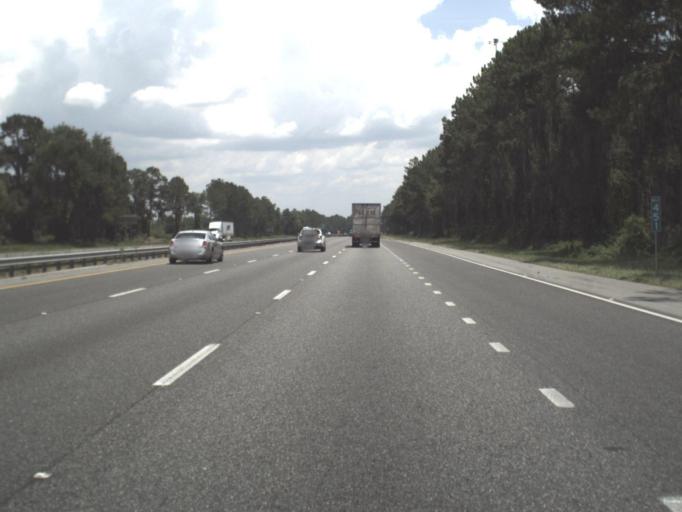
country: US
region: Florida
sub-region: Hamilton County
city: Jasper
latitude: 30.4457
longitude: -82.9284
